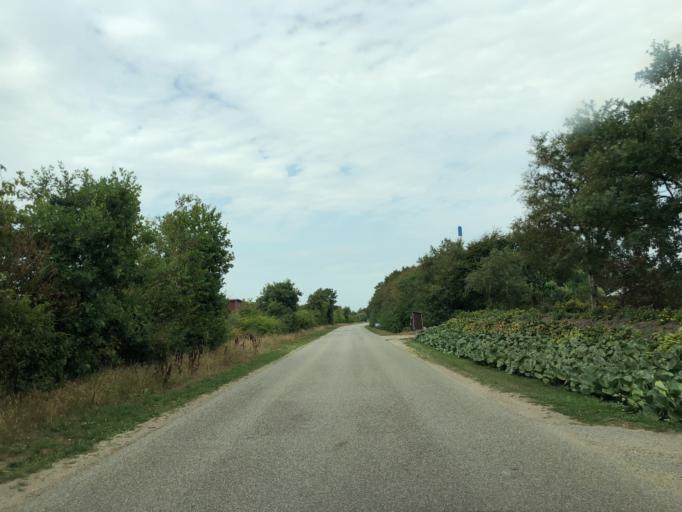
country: DK
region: Central Jutland
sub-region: Holstebro Kommune
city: Ulfborg
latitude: 56.1916
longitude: 8.3133
